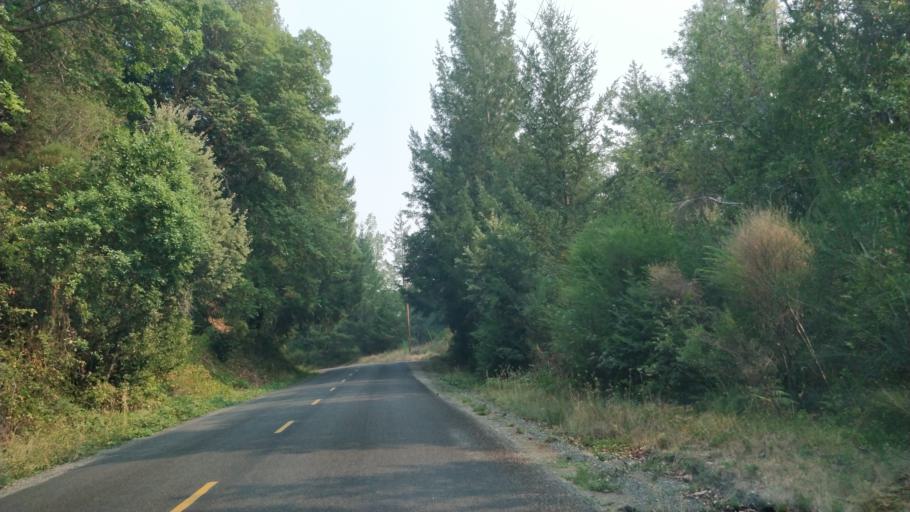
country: US
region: California
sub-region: Humboldt County
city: Rio Dell
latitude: 40.2697
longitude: -124.2188
